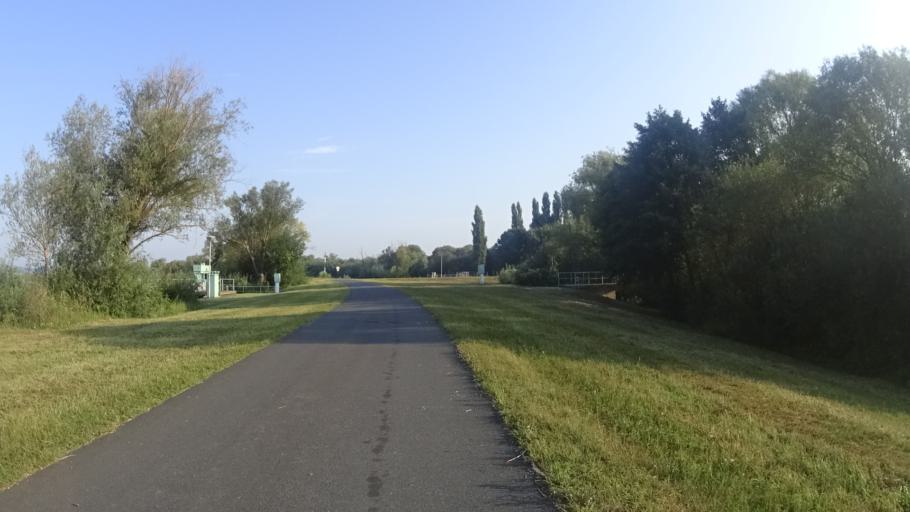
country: HU
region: Zala
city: Sarmellek
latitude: 46.6346
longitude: 17.1730
